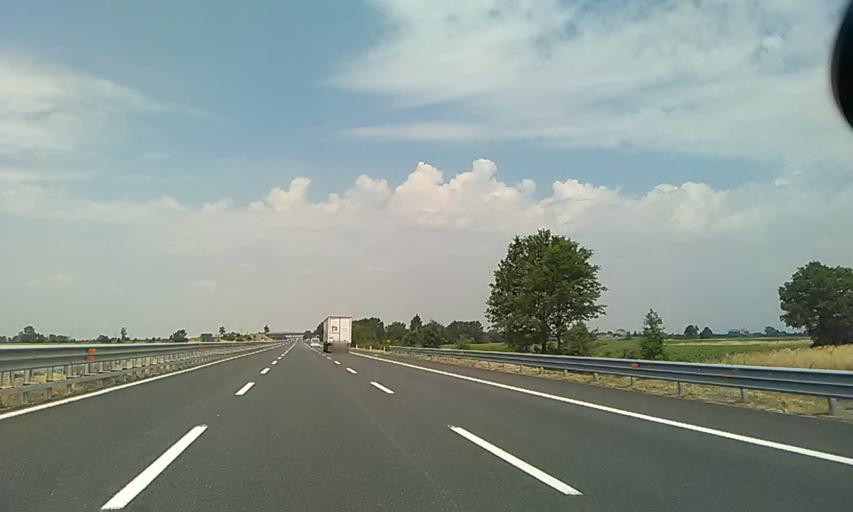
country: IT
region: Piedmont
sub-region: Provincia di Alessandria
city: Predosa
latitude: 44.7753
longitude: 8.6267
